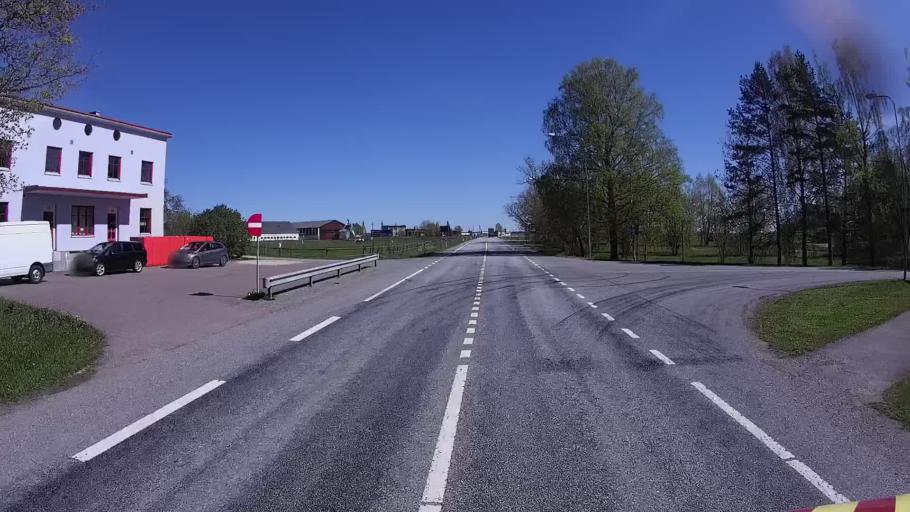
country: EE
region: Laeaene-Virumaa
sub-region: Tapa vald
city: Tapa
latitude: 59.2456
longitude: 25.6887
